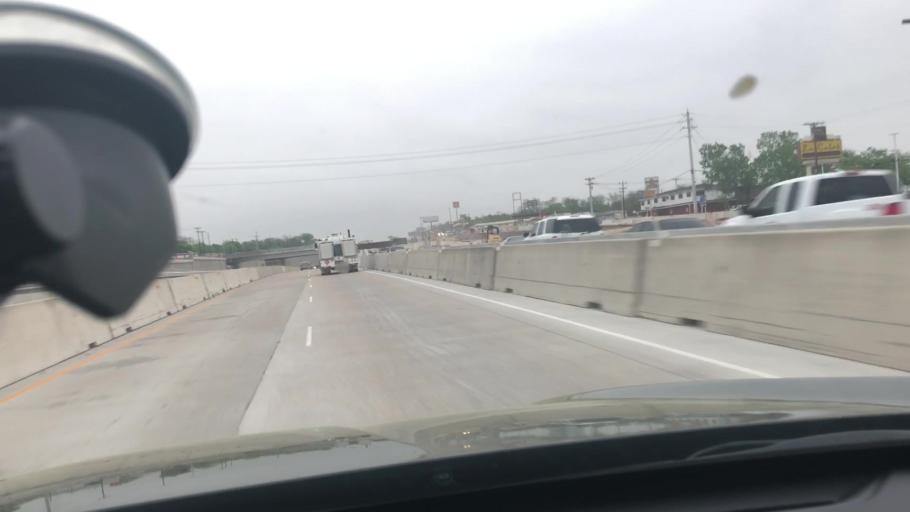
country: US
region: Texas
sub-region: Bell County
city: Temple
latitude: 31.0932
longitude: -97.3793
